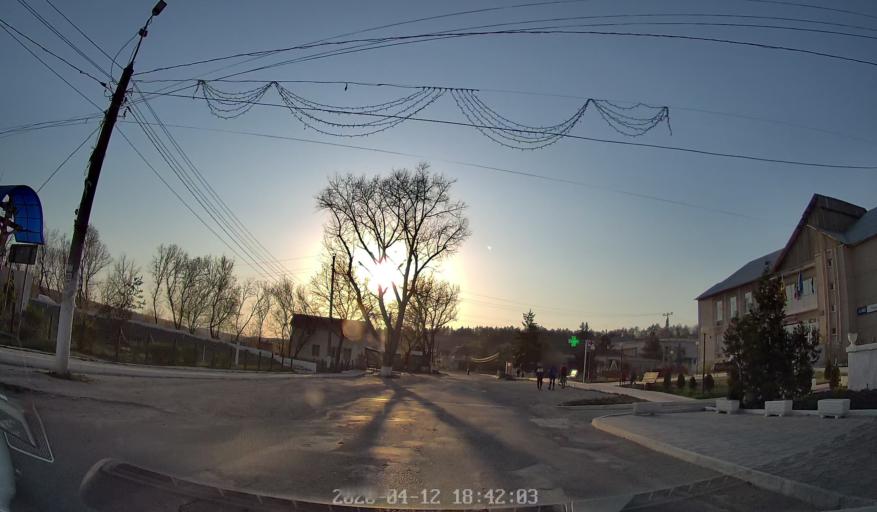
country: MD
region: Chisinau
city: Ciorescu
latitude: 47.1358
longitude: 28.9423
